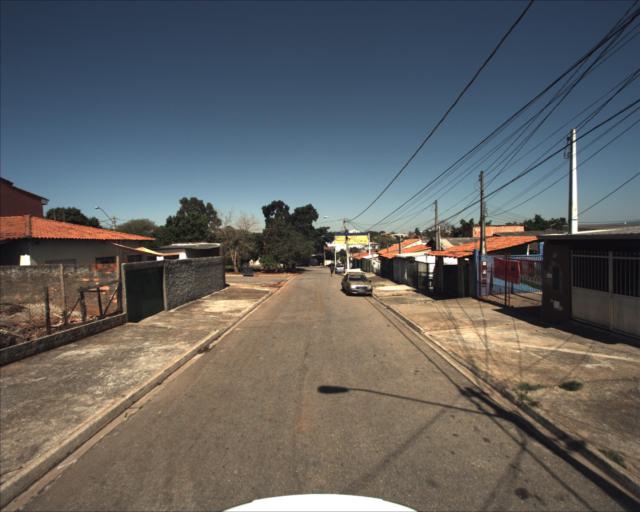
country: BR
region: Sao Paulo
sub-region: Sorocaba
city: Sorocaba
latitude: -23.4671
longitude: -47.4886
